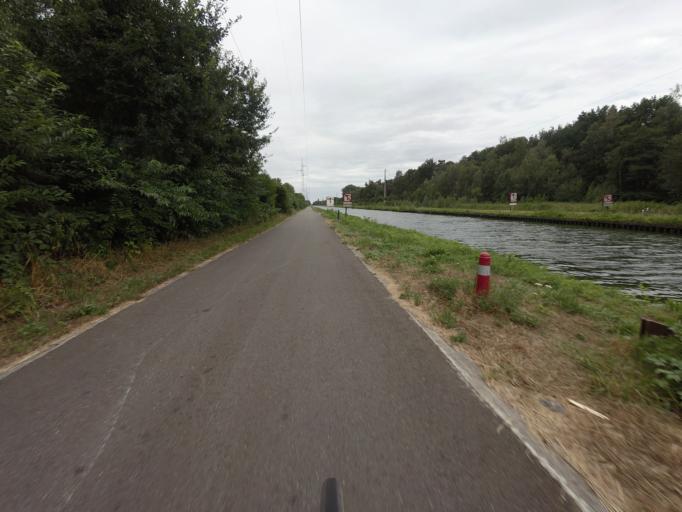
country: BE
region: Flanders
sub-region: Provincie Antwerpen
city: Brasschaat
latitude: 51.2857
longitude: 4.5382
